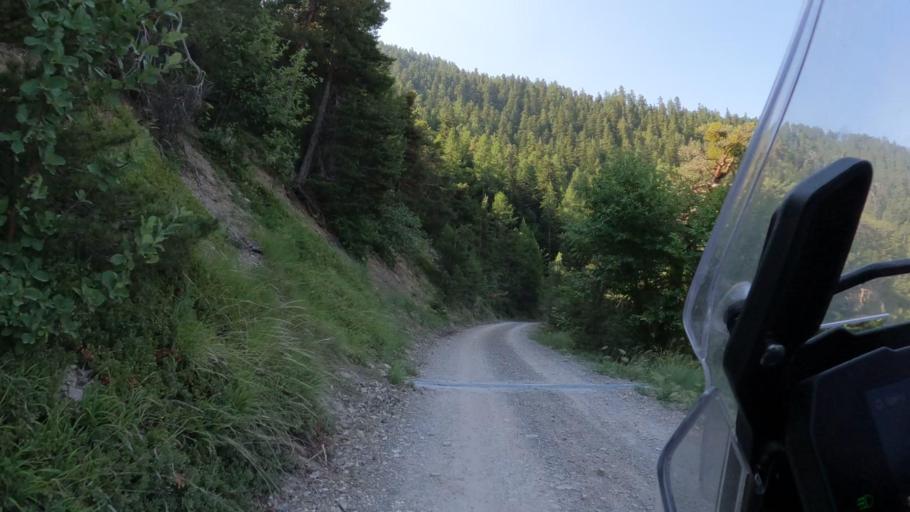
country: FR
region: Provence-Alpes-Cote d'Azur
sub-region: Departement des Hautes-Alpes
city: Embrun
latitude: 44.5890
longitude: 6.5603
